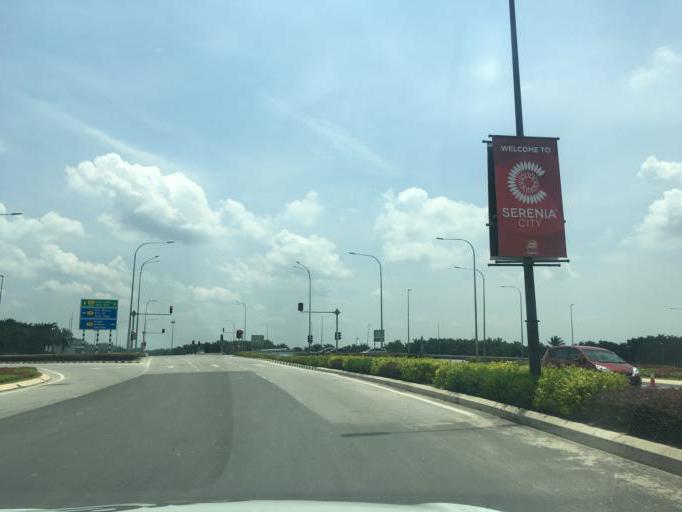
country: MY
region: Putrajaya
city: Putrajaya
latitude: 2.8502
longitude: 101.6960
